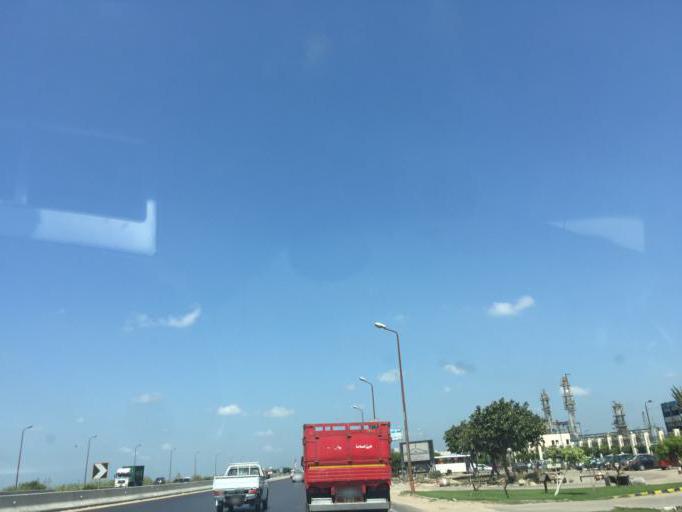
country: EG
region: Alexandria
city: Alexandria
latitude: 31.1046
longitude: 29.8651
